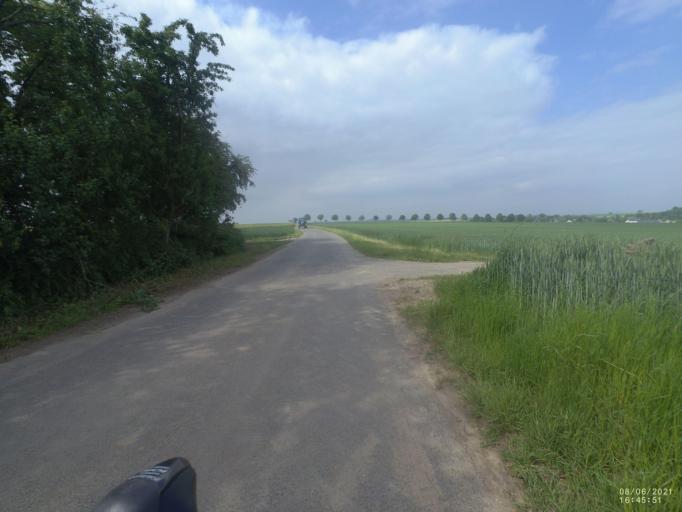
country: DE
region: Rheinland-Pfalz
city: Kalt
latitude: 50.2485
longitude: 7.3872
